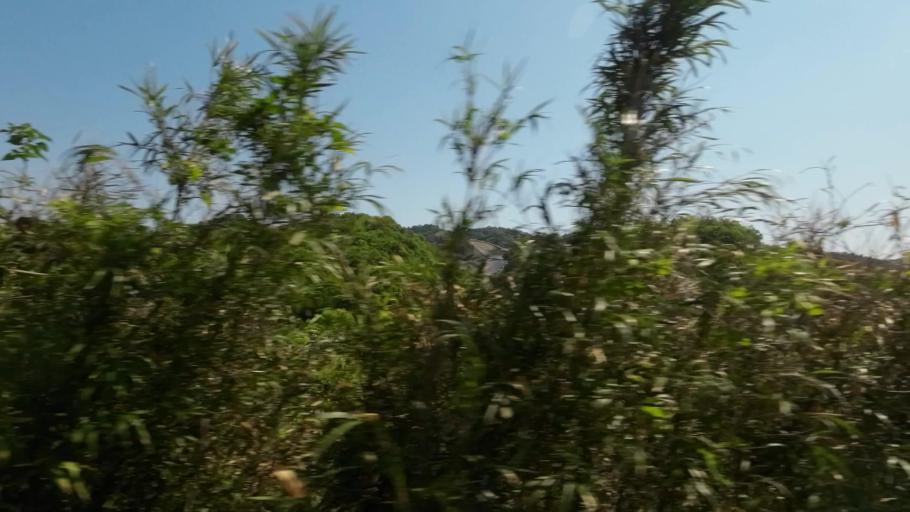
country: JP
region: Ehime
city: Niihama
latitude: 33.9676
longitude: 133.3588
